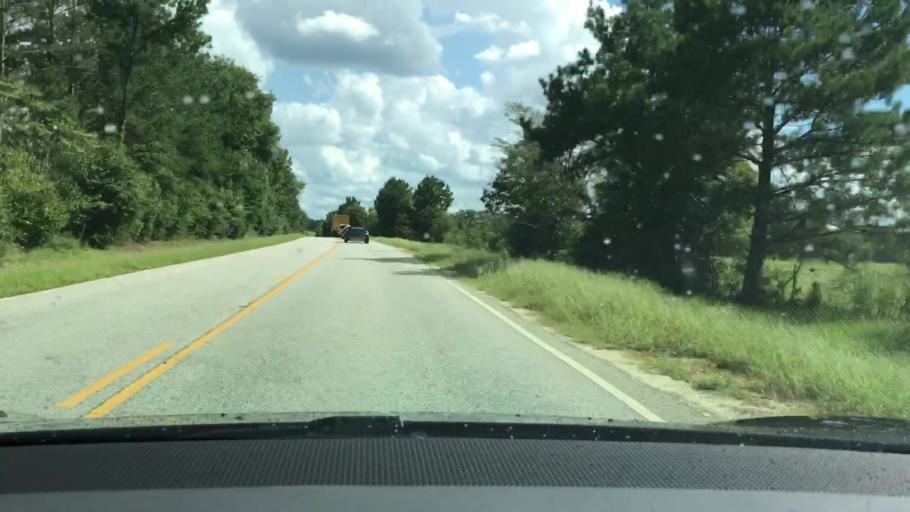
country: US
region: Alabama
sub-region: Montgomery County
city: Pike Road
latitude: 32.2278
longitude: -86.0926
